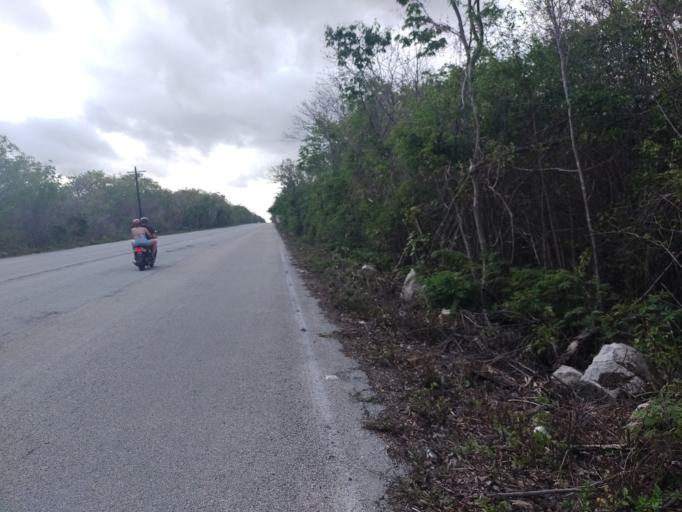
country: MX
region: Quintana Roo
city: San Miguel de Cozumel
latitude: 20.4337
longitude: -86.8552
